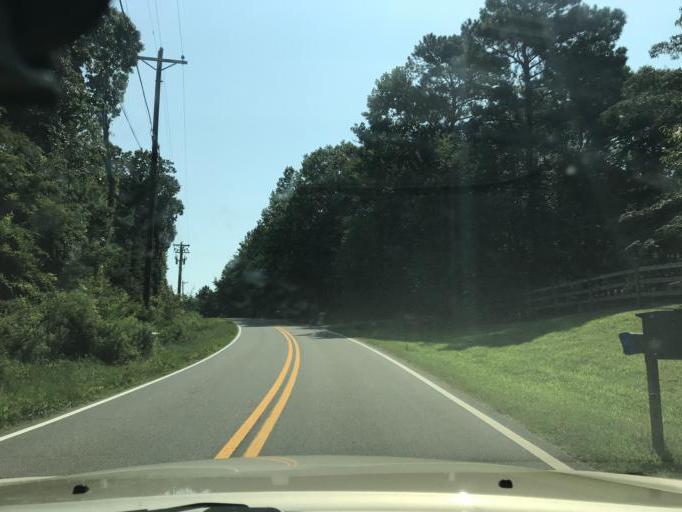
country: US
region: Georgia
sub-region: Hall County
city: Flowery Branch
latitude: 34.2321
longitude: -84.0002
